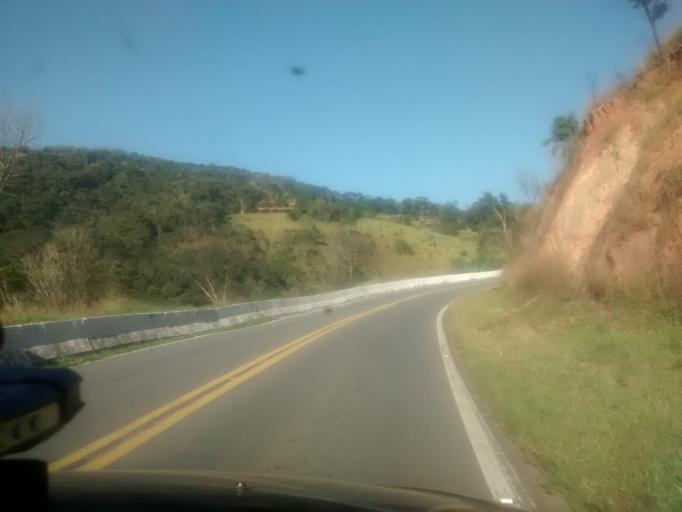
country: BR
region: Sao Paulo
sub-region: Campos Do Jordao
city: Campos do Jordao
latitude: -22.8281
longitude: -45.7106
